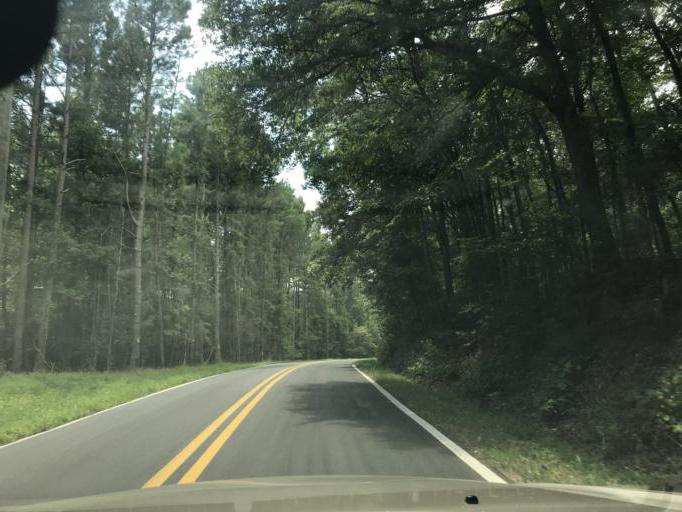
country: US
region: Georgia
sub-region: Dawson County
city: Dawsonville
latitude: 34.3269
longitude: -84.2131
